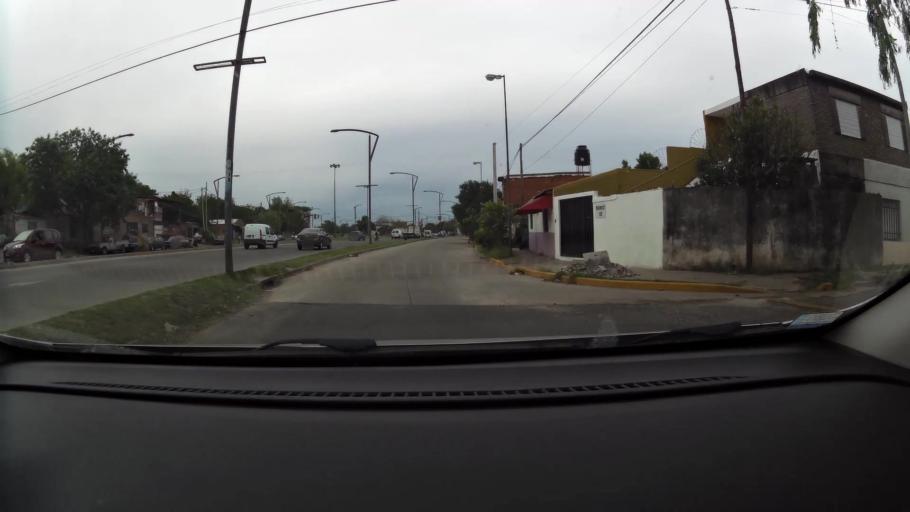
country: AR
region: Santa Fe
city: Granadero Baigorria
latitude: -32.9127
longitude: -60.6919
